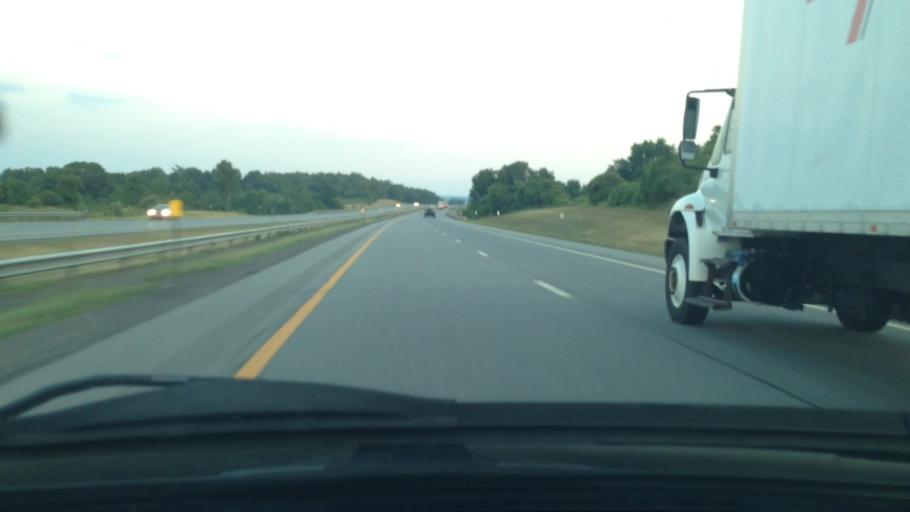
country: US
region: New York
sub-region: Montgomery County
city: Saint Johnsville
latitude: 42.9782
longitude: -74.6548
